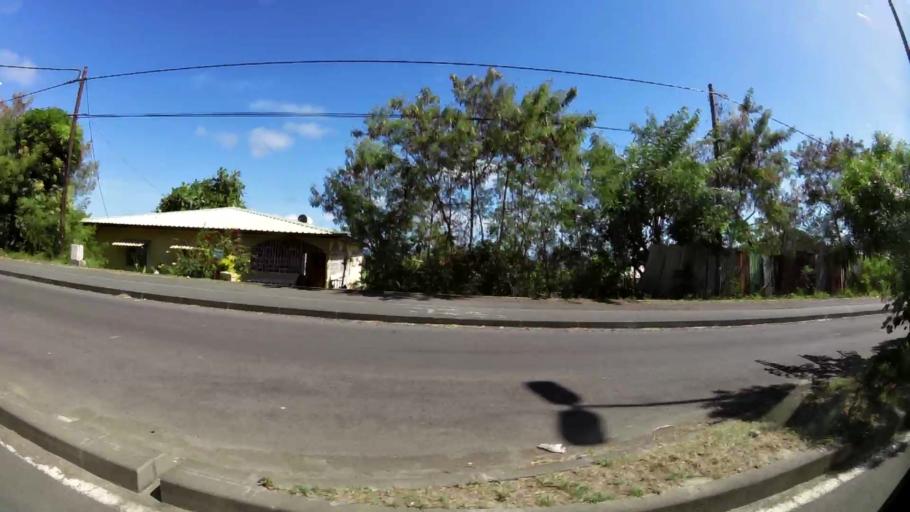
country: YT
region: Pamandzi
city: Pamandzi
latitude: -12.7953
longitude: 45.2832
